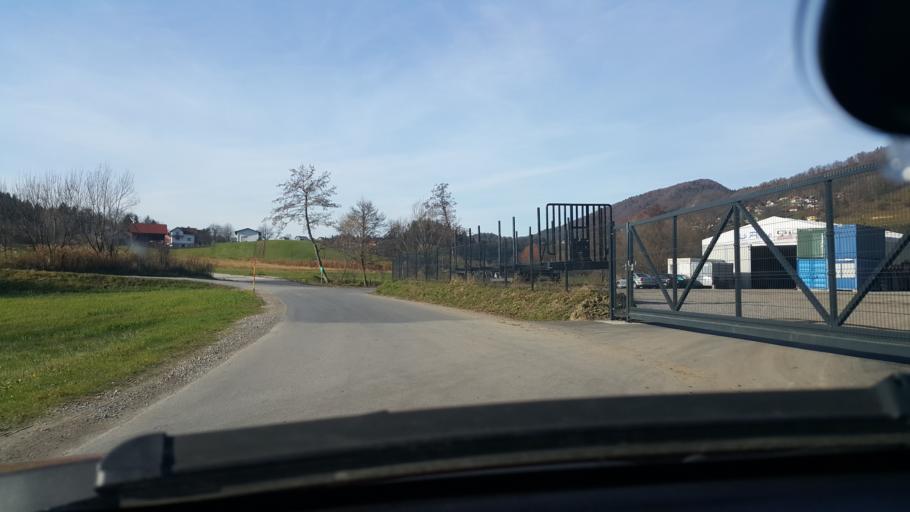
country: SI
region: Velenje
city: Velenje
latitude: 46.3444
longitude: 15.1661
